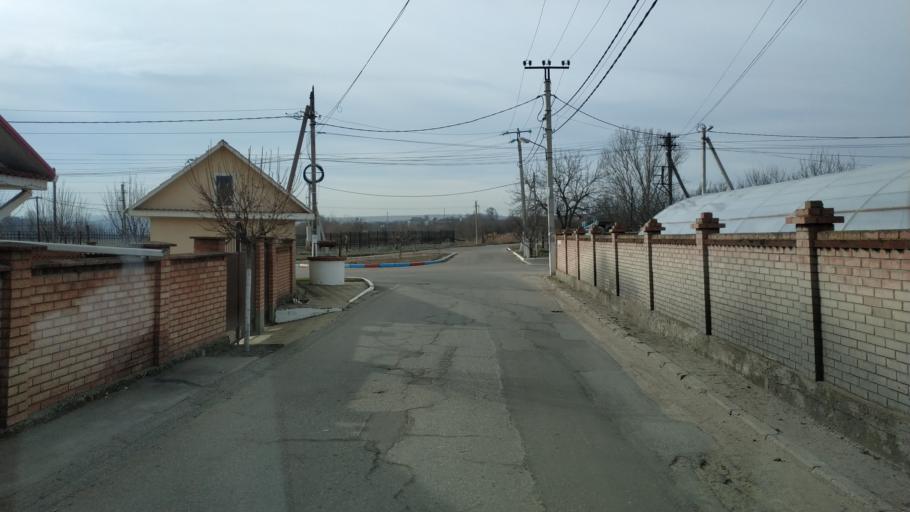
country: MD
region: Chisinau
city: Vatra
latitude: 47.0882
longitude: 28.7685
